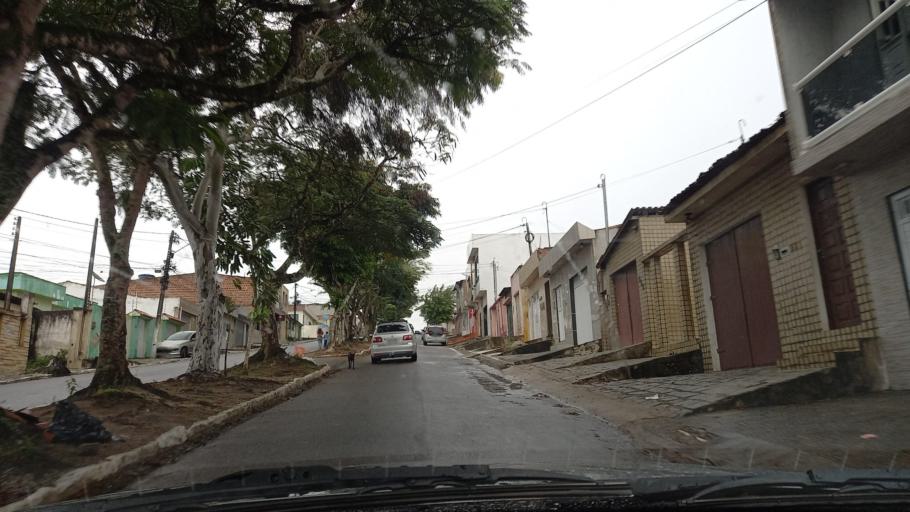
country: BR
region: Pernambuco
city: Garanhuns
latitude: -8.8799
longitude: -36.4984
